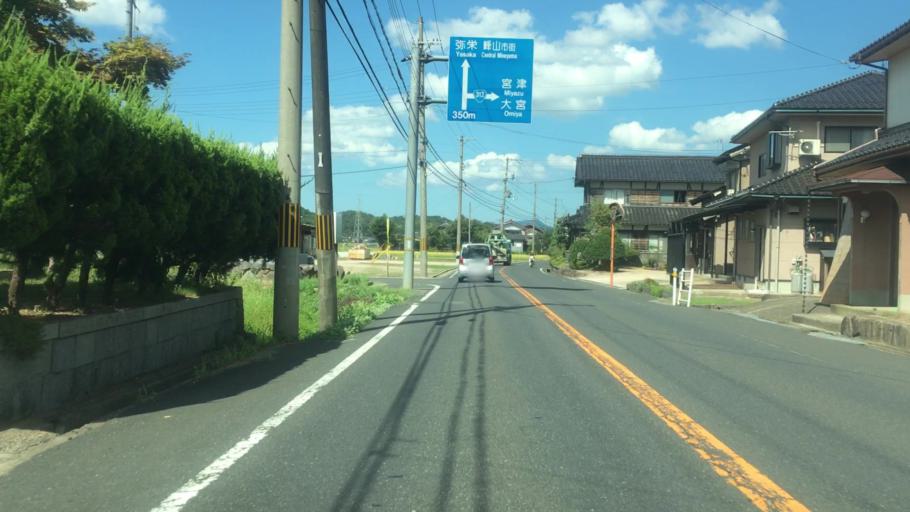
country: JP
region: Kyoto
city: Miyazu
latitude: 35.5981
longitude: 135.0452
